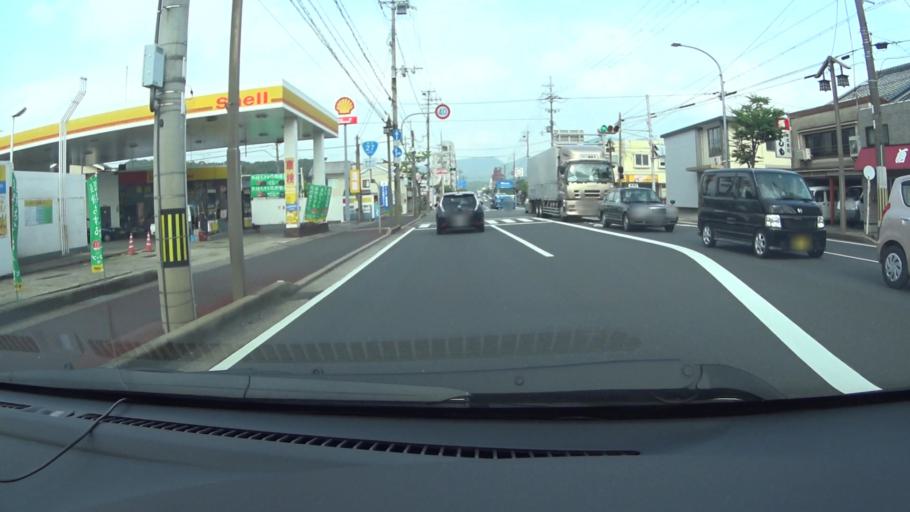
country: JP
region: Kyoto
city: Maizuru
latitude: 35.4508
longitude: 135.3295
